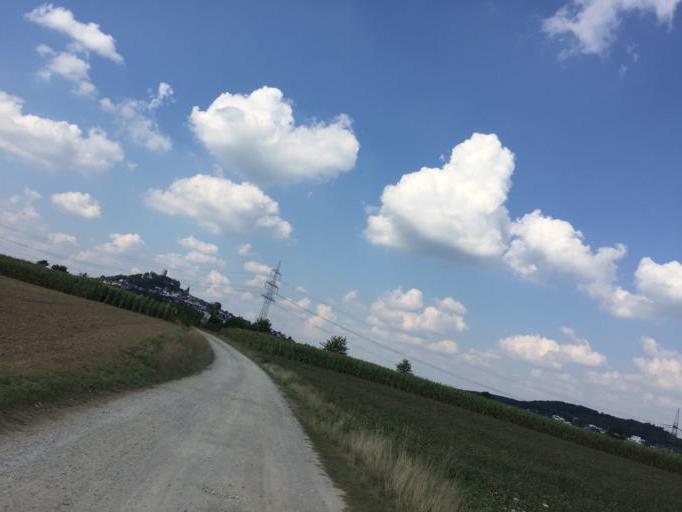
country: DE
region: Hesse
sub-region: Regierungsbezirk Giessen
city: Heuchelheim
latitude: 50.6036
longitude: 8.6456
